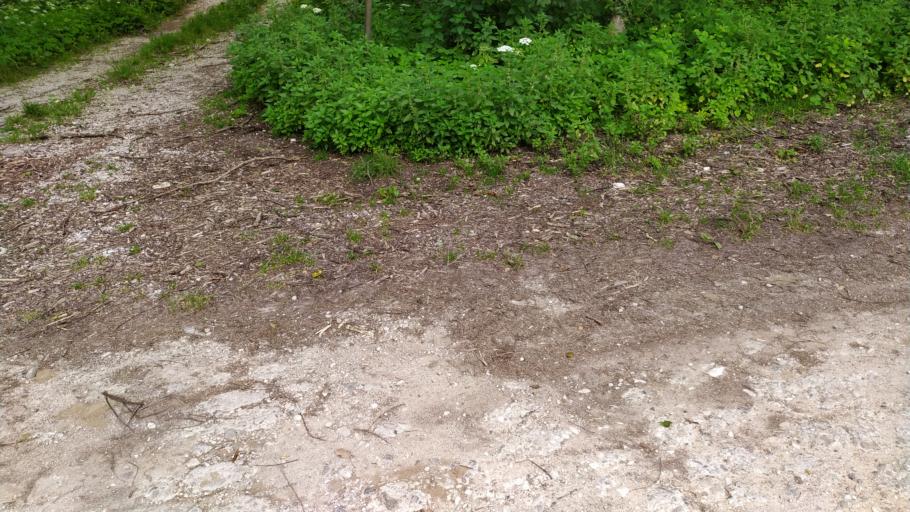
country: IT
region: Friuli Venezia Giulia
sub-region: Provincia di Udine
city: Osoppo
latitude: 46.2443
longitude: 13.0694
